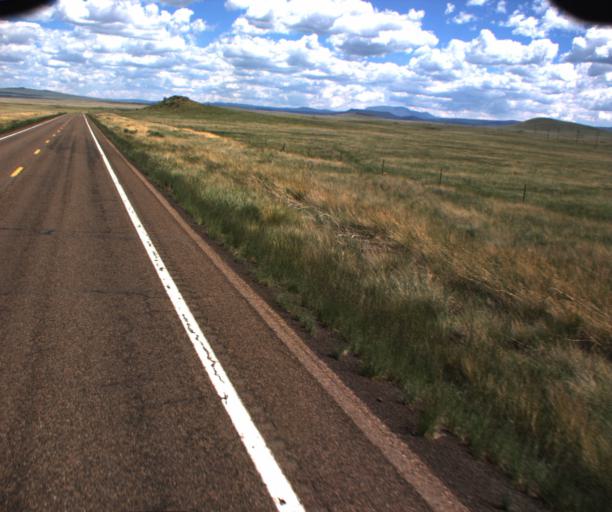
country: US
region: Arizona
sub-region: Apache County
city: Springerville
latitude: 34.2041
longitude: -109.4099
